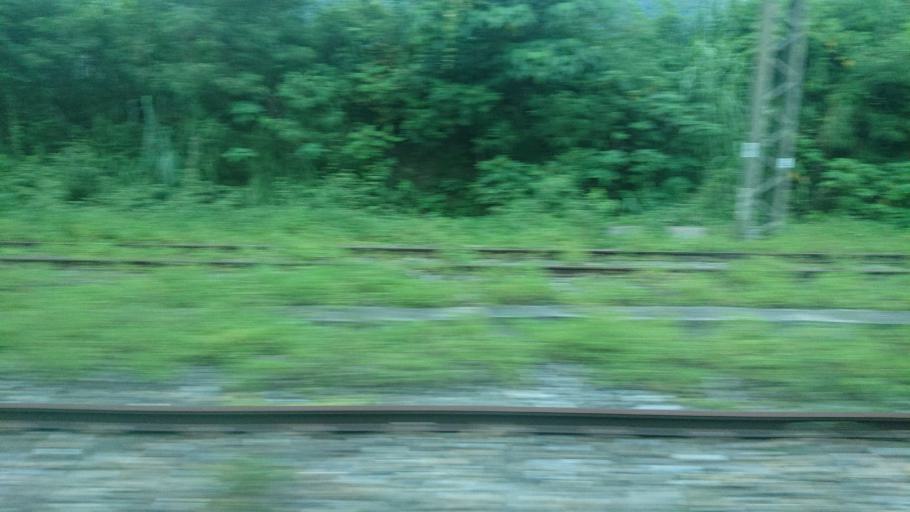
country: TW
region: Taiwan
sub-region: Hualien
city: Hualian
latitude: 24.1226
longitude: 121.6374
